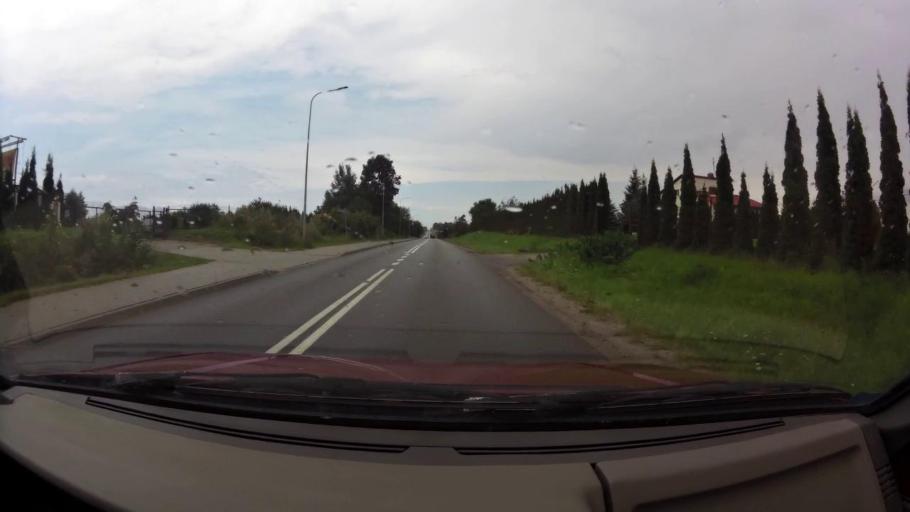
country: PL
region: West Pomeranian Voivodeship
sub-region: Koszalin
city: Koszalin
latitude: 54.1628
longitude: 16.1498
